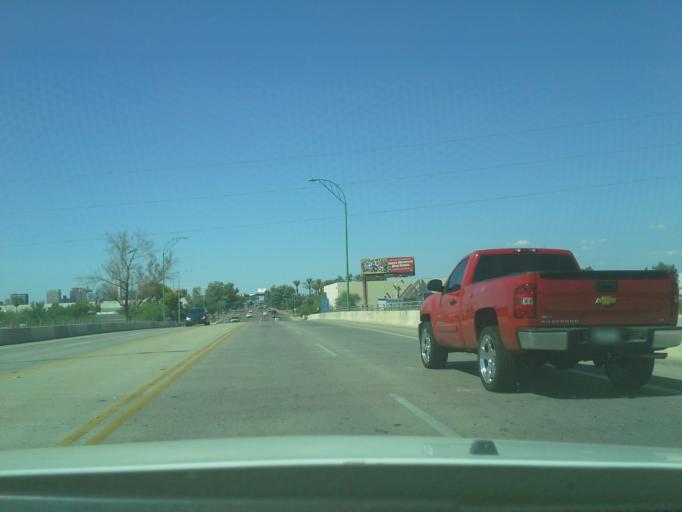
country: US
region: Arizona
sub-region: Maricopa County
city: Phoenix
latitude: 33.4208
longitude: -112.0648
